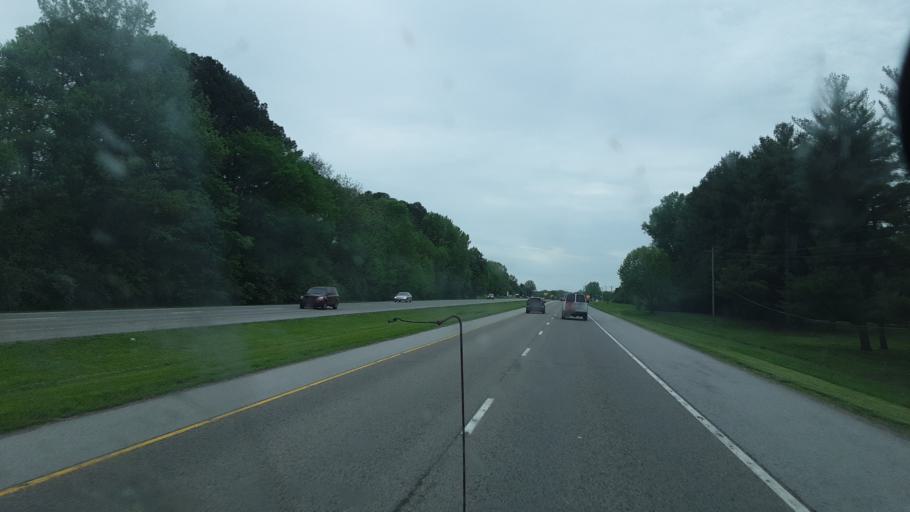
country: US
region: Illinois
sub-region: Jackson County
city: Carbondale
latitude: 37.7436
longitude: -89.2578
